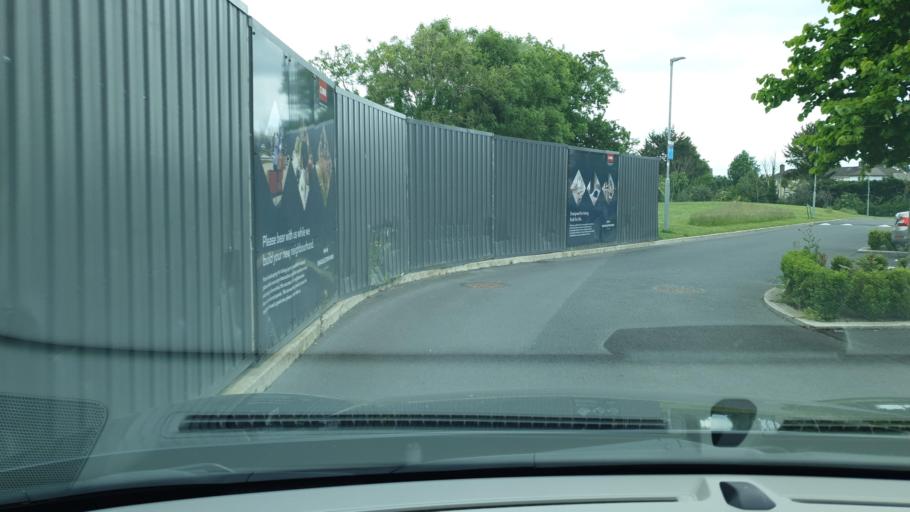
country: IE
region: Leinster
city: Lucan
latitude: 53.3476
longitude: -6.4728
